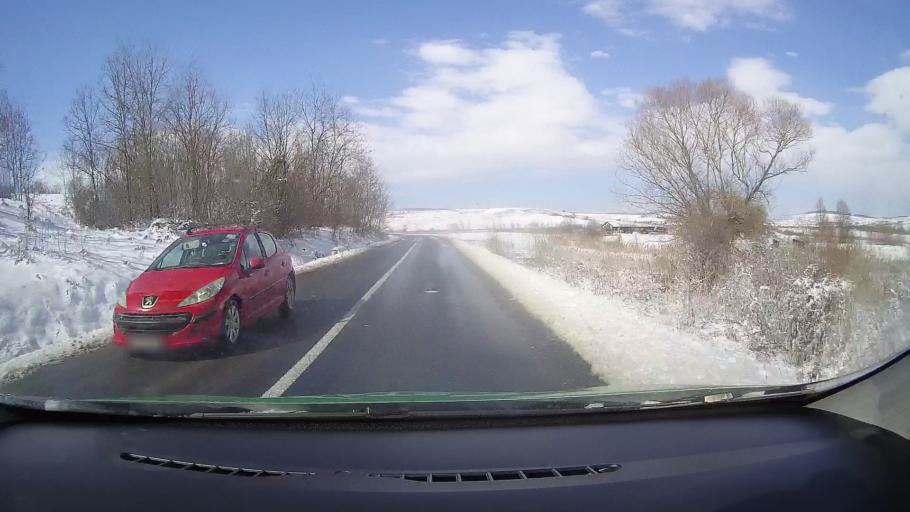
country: RO
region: Sibiu
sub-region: Comuna Nocrich
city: Nocrich
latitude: 45.9085
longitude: 24.4626
